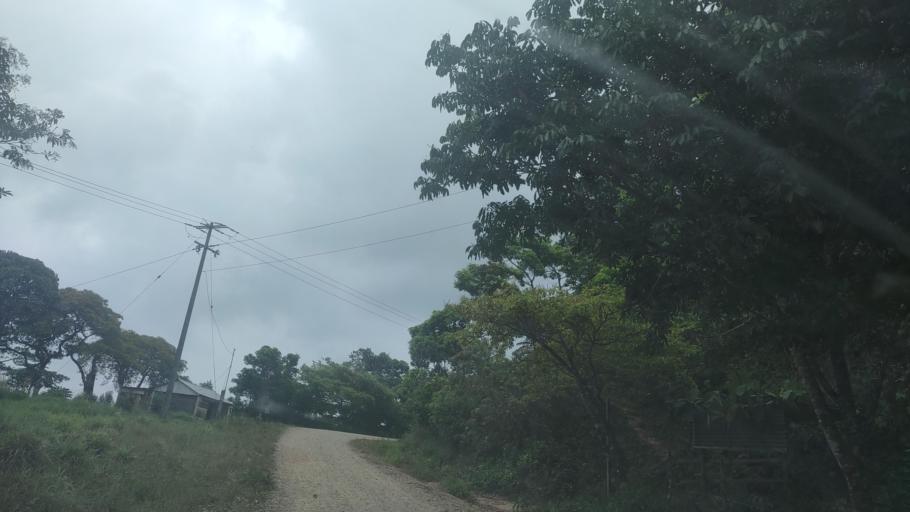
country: MX
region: Tabasco
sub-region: Huimanguillo
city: Francisco Rueda
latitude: 17.4383
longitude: -94.0239
